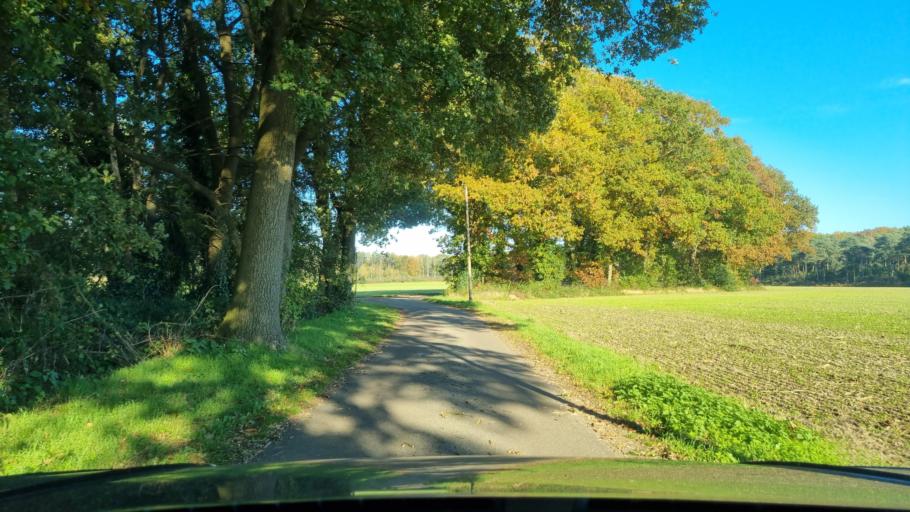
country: DE
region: North Rhine-Westphalia
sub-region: Regierungsbezirk Dusseldorf
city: Kranenburg
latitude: 51.7706
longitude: 6.0566
